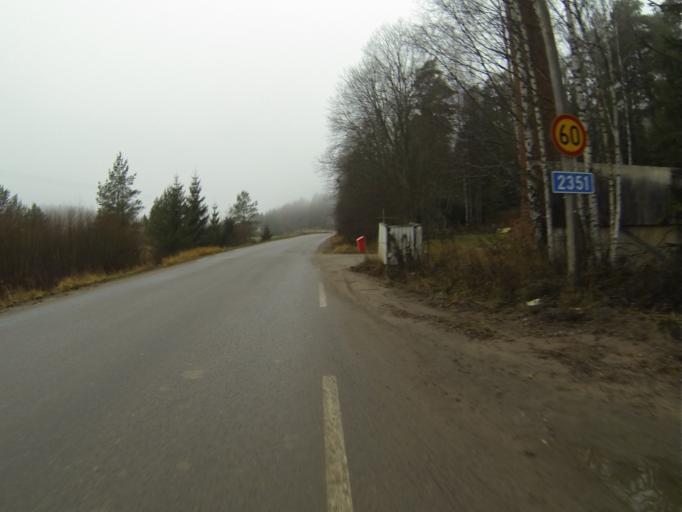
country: FI
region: Varsinais-Suomi
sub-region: Salo
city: Halikko
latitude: 60.4165
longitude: 22.9257
